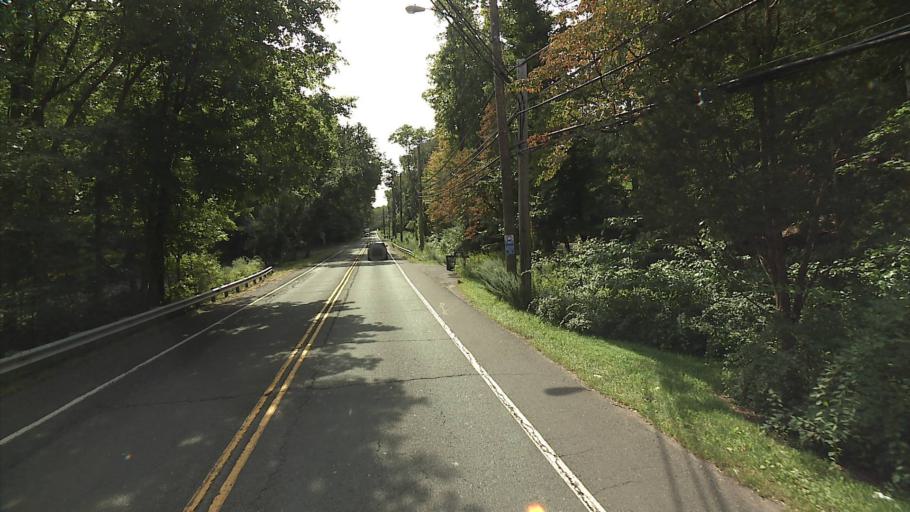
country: US
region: Connecticut
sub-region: Fairfield County
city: North Stamford
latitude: 41.1240
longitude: -73.5733
